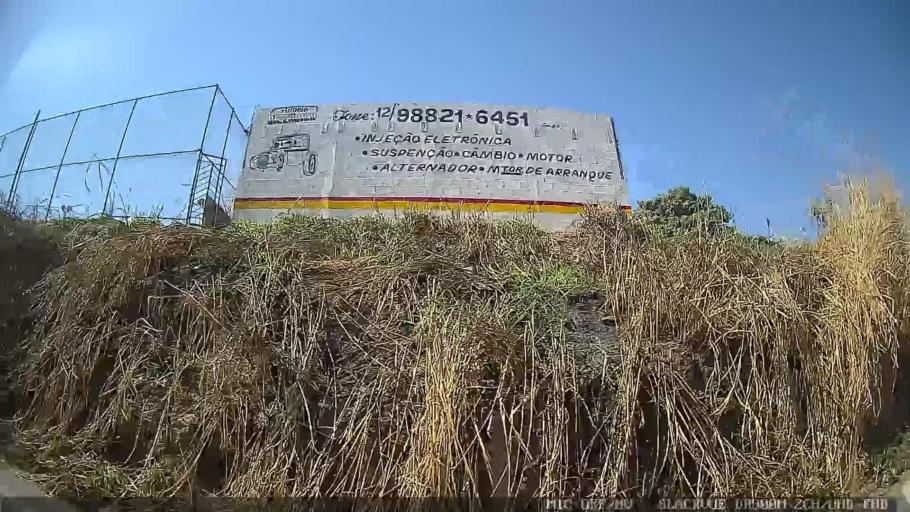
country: BR
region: Sao Paulo
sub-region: Jacarei
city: Jacarei
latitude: -23.3368
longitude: -46.0021
